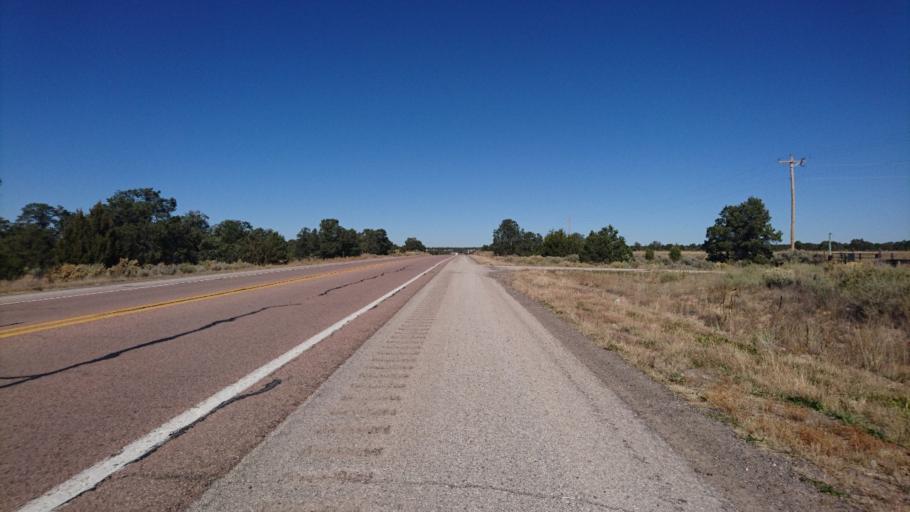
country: US
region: New Mexico
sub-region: McKinley County
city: Gallup
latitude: 35.3328
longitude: -108.7578
